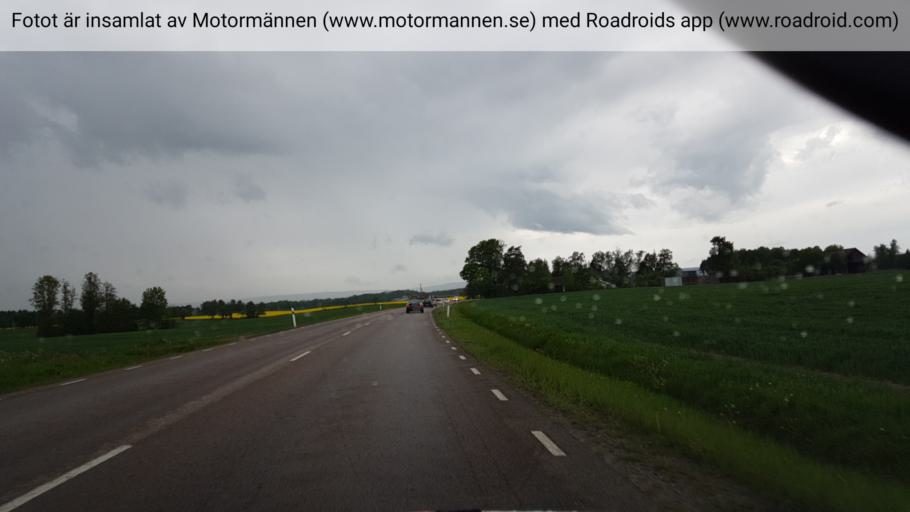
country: SE
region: Vaestra Goetaland
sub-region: Tidaholms Kommun
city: Olofstorp
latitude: 58.3726
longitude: 13.9924
